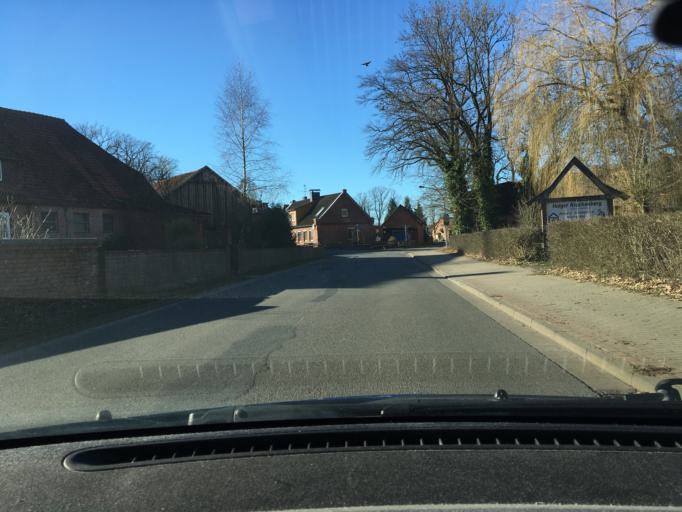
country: DE
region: Lower Saxony
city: Ebstorf
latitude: 53.0188
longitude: 10.4003
